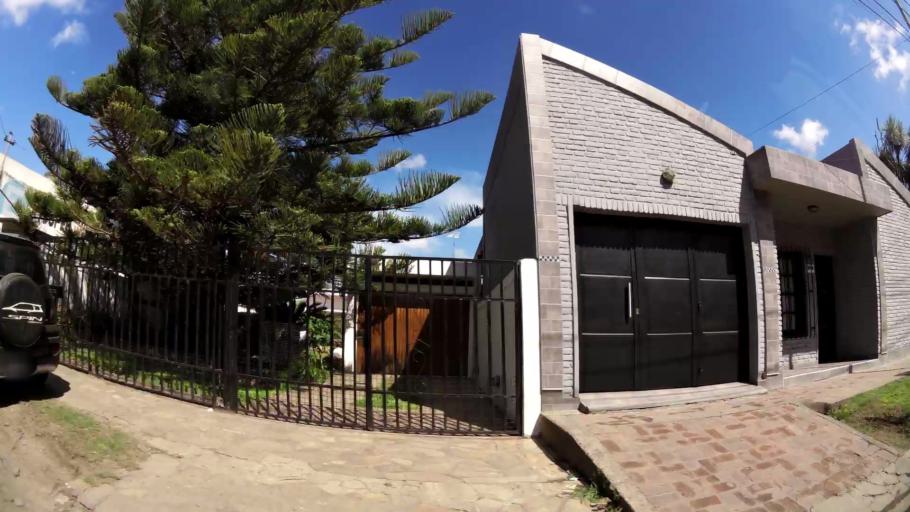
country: AR
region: Buenos Aires
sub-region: Partido de Quilmes
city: Quilmes
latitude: -34.8144
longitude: -58.2628
